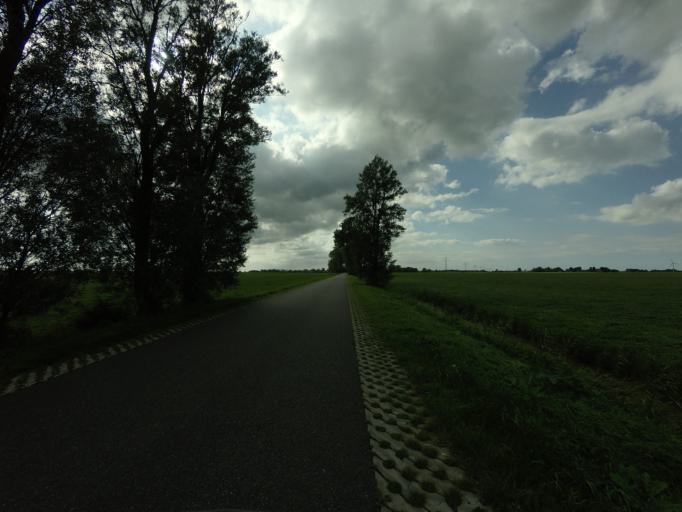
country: NL
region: Friesland
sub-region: Gemeente Littenseradiel
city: Wommels
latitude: 53.0686
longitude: 5.5810
